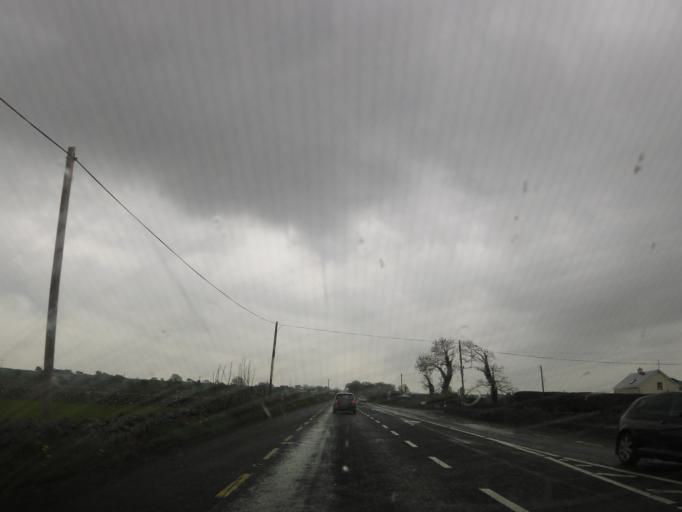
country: IE
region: Connaught
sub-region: County Galway
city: Tuam
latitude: 53.4659
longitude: -8.9092
